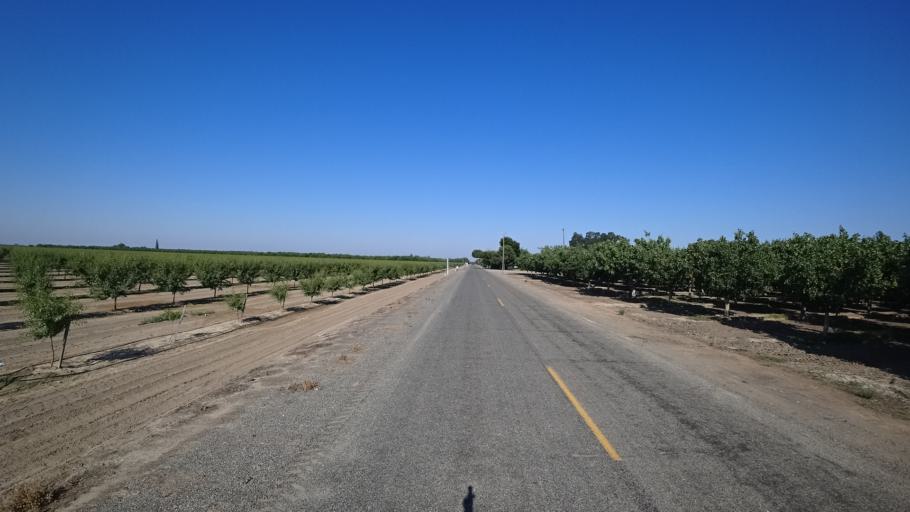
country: US
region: California
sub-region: Kings County
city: Lucerne
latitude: 36.3862
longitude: -119.6946
